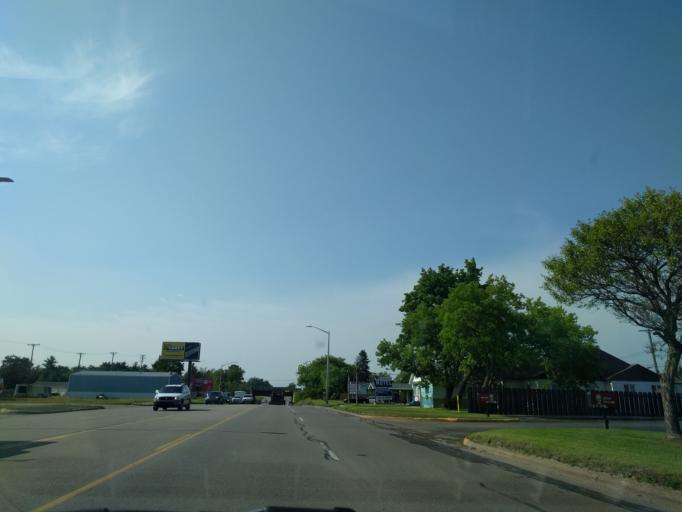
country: US
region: Michigan
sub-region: Delta County
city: Escanaba
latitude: 45.7650
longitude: -87.0778
